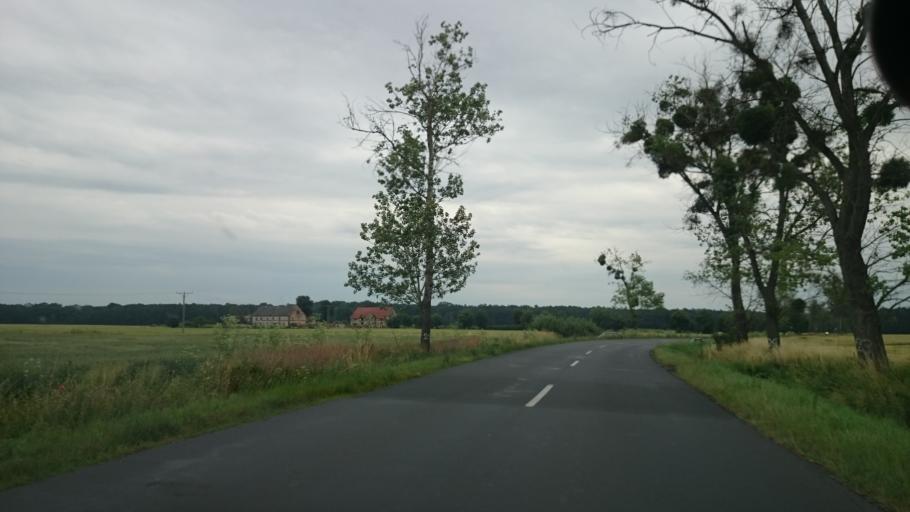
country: PL
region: Opole Voivodeship
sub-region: Powiat brzeski
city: Grodkow
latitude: 50.6739
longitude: 17.4151
